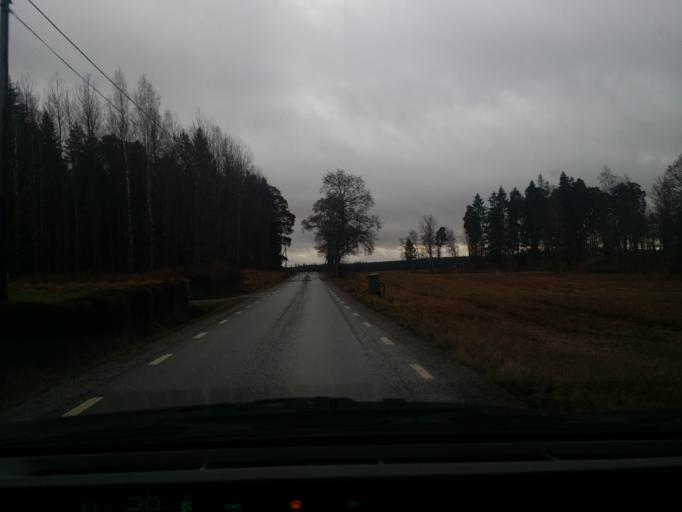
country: SE
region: Vaestmanland
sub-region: Vasteras
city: Skultuna
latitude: 59.7822
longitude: 16.3874
